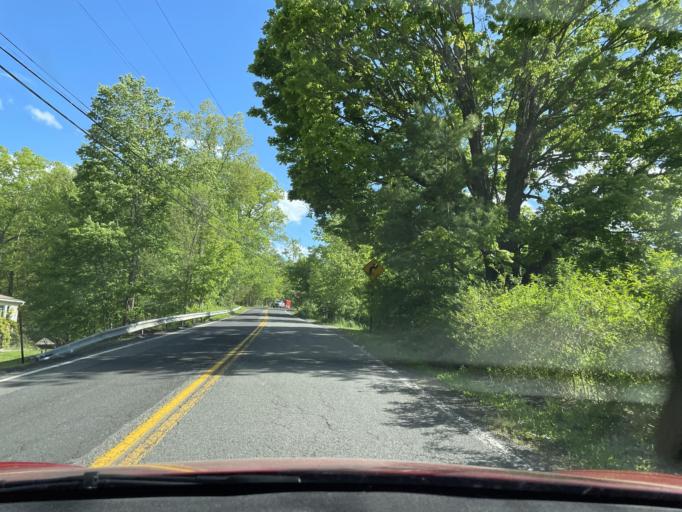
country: US
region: New York
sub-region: Ulster County
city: Zena
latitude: 41.9995
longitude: -74.0822
